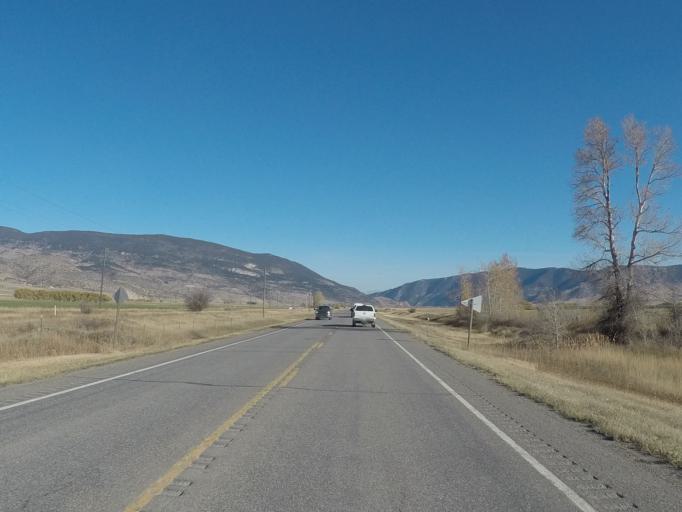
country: US
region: Montana
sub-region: Park County
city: Livingston
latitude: 45.5270
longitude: -110.6067
